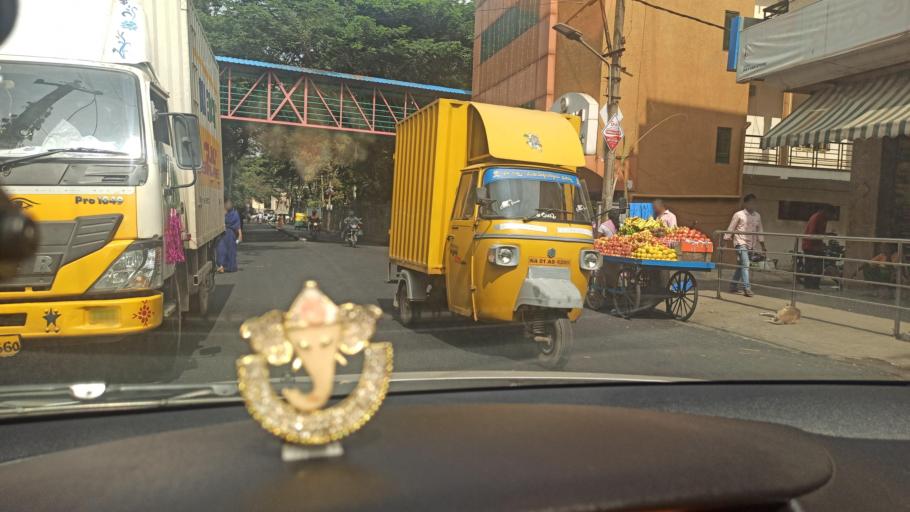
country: IN
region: Karnataka
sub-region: Bangalore Urban
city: Bangalore
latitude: 12.9235
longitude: 77.6340
